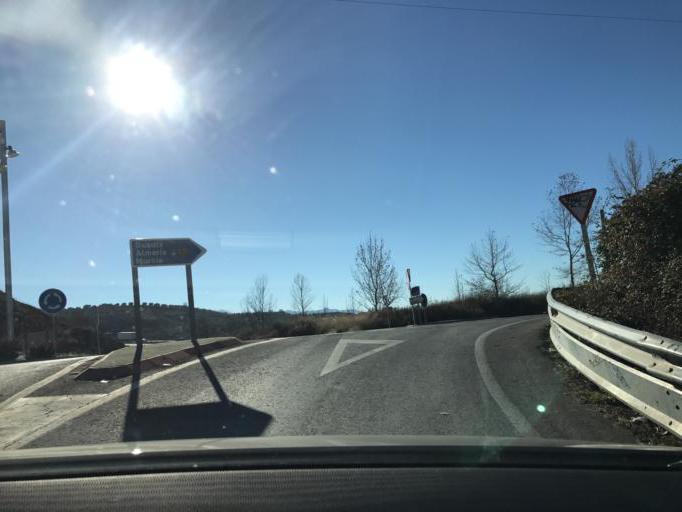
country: ES
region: Andalusia
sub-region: Provincia de Granada
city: Alfacar
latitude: 37.2335
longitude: -3.5691
